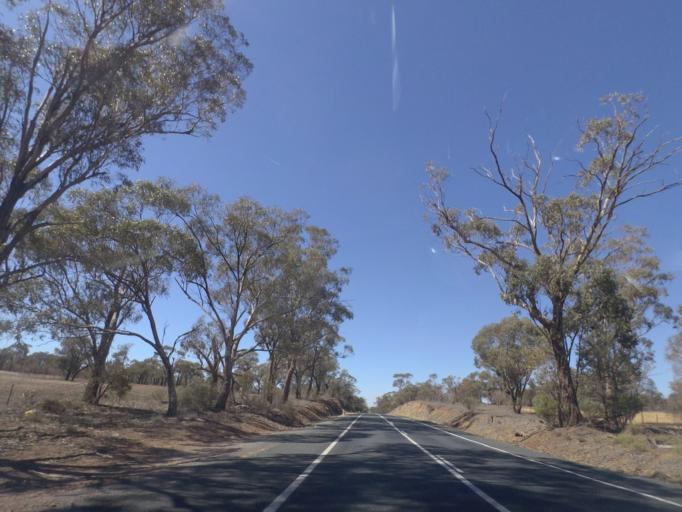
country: AU
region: New South Wales
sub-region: Bland
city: West Wyalong
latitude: -34.1661
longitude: 147.1159
